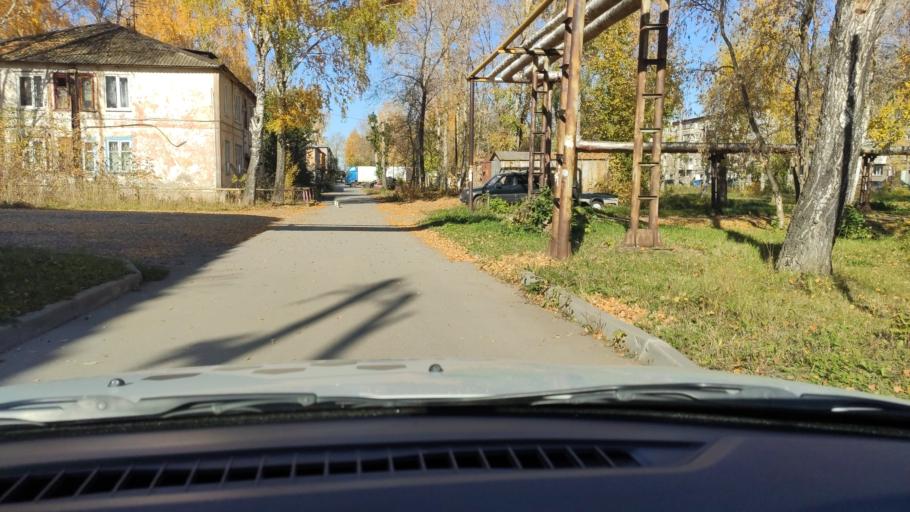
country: RU
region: Perm
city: Kondratovo
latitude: 57.9508
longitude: 56.1154
